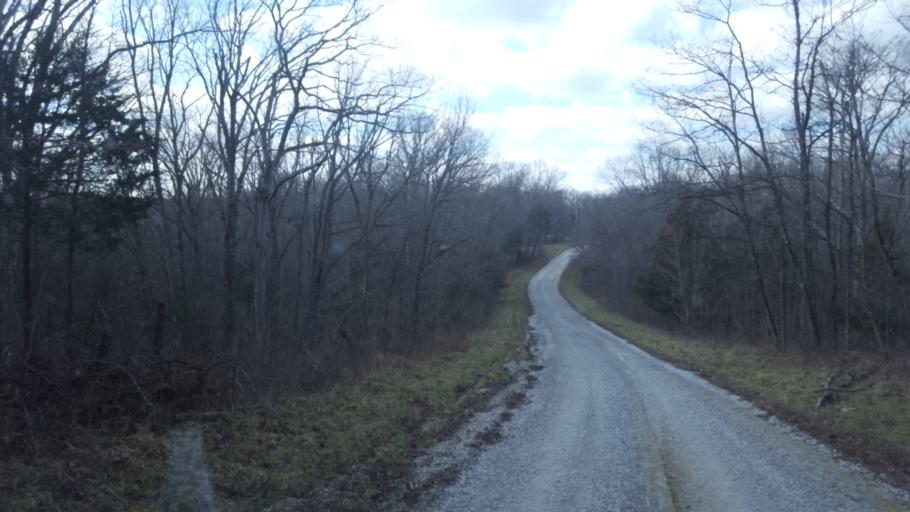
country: US
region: Kentucky
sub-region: Owen County
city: Owenton
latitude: 38.3822
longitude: -84.9184
